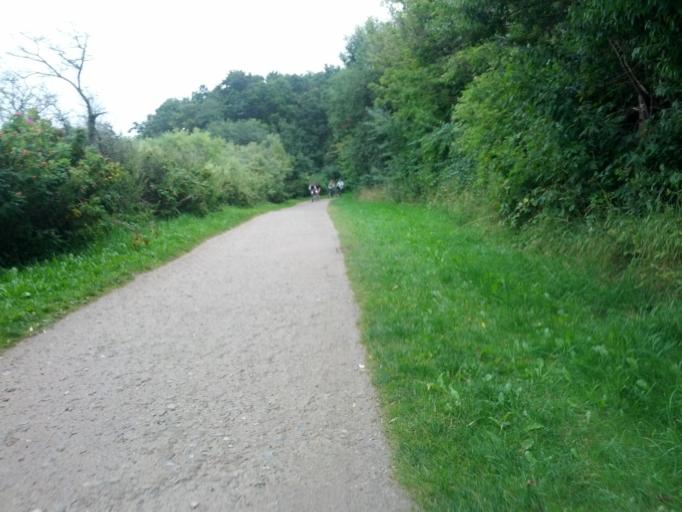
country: DE
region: Mecklenburg-Vorpommern
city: Ostseebad Kuhlungsborn
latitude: 54.1448
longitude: 11.8159
